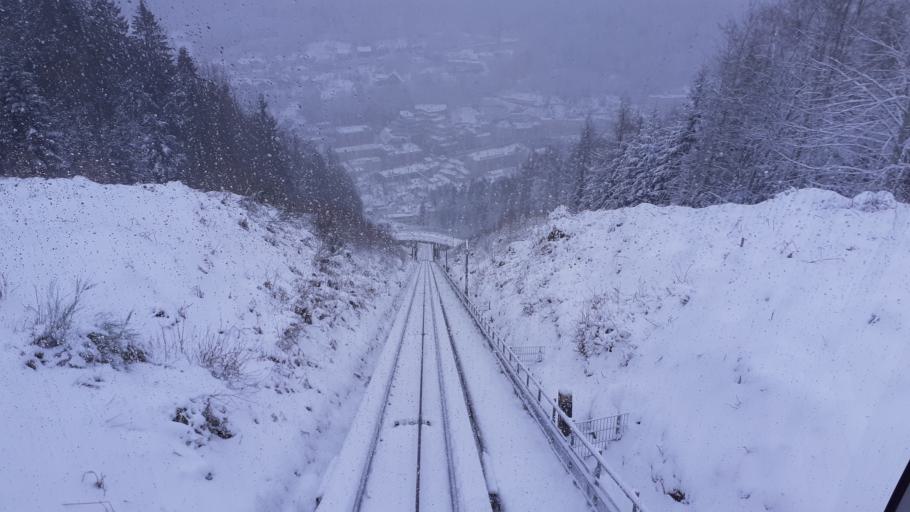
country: DE
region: Baden-Wuerttemberg
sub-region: Karlsruhe Region
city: Bad Wildbad
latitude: 48.7506
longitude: 8.5398
